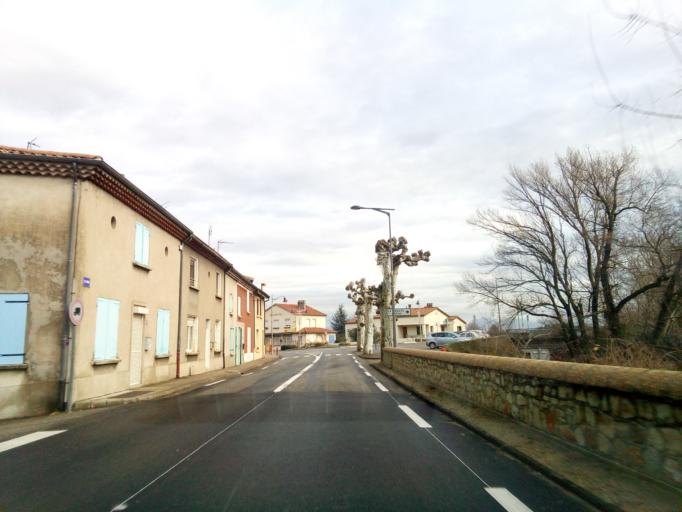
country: FR
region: Rhone-Alpes
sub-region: Departement de l'Ardeche
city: Beauchastel
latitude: 44.8252
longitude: 4.7992
